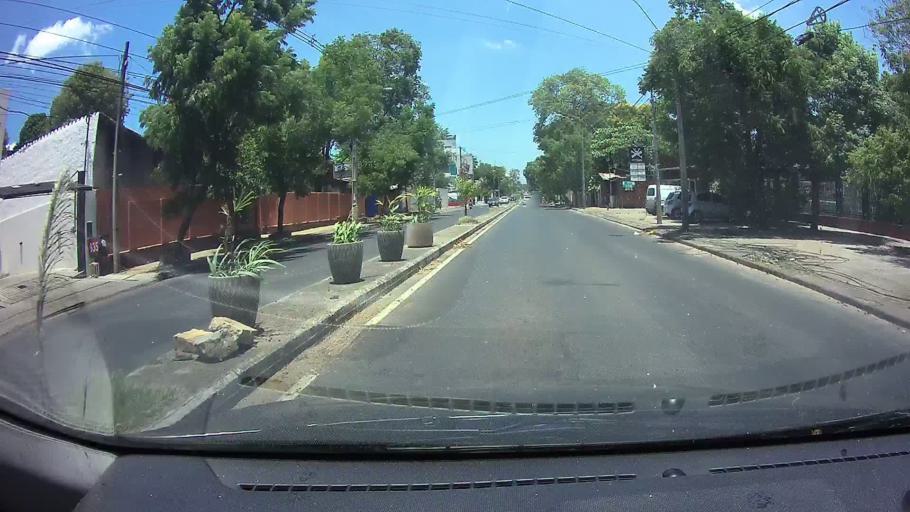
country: PY
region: Asuncion
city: Asuncion
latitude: -25.2972
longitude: -57.5930
